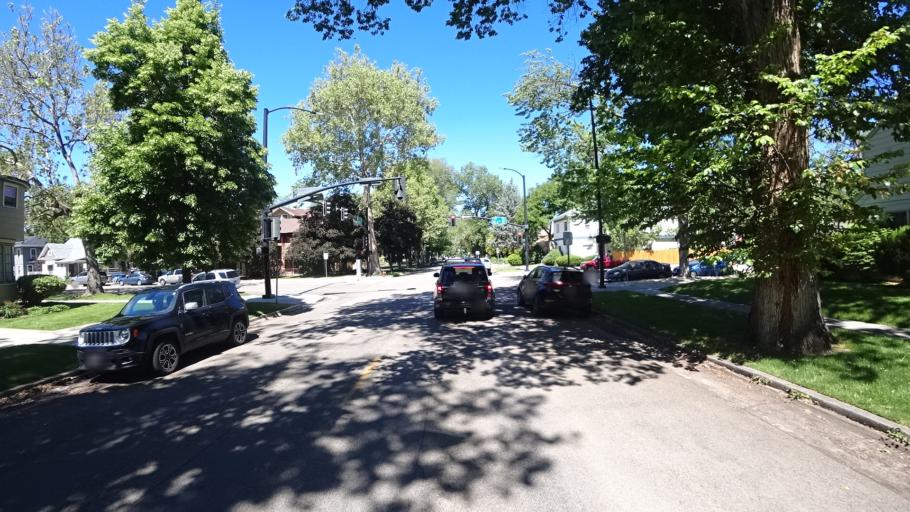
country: US
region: Idaho
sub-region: Ada County
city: Boise
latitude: 43.6196
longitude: -116.1957
